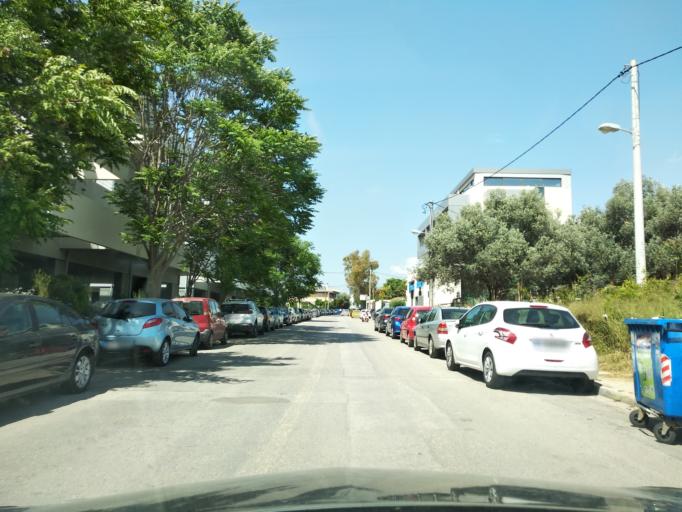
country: GR
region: Attica
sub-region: Nomarchia Athinas
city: Marousi
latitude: 38.0410
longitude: 23.7999
